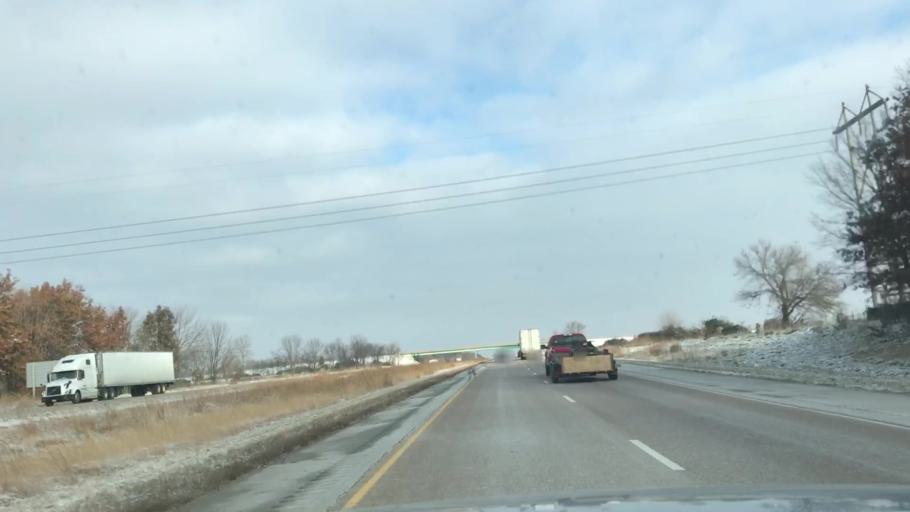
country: US
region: Illinois
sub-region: Macoupin County
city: Mount Olive
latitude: 39.0391
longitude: -89.7554
